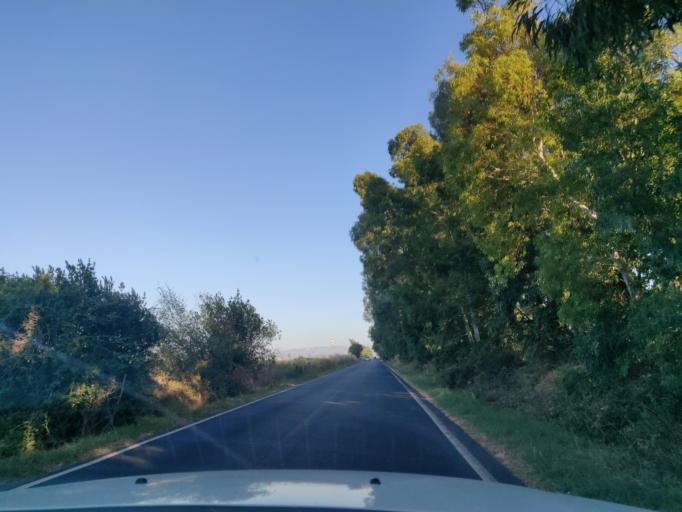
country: IT
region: Latium
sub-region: Provincia di Viterbo
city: Tarquinia
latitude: 42.2694
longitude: 11.6915
